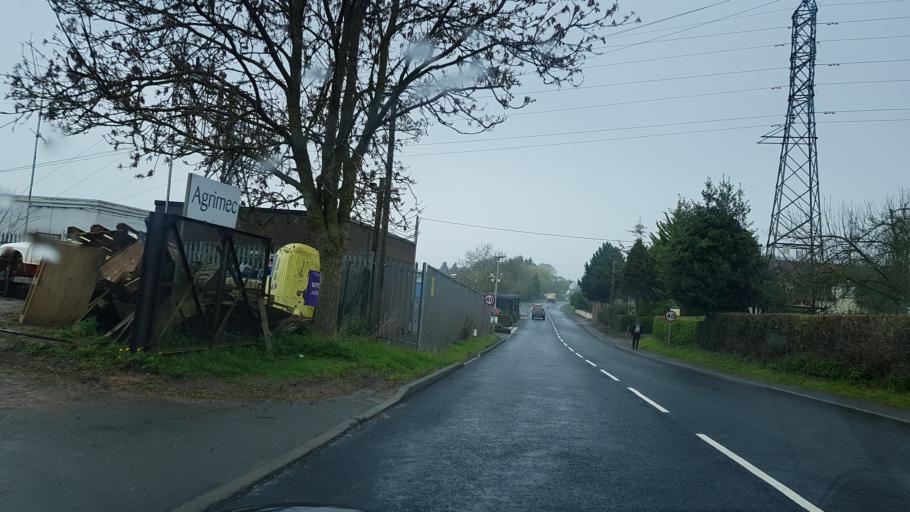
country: GB
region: England
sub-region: Herefordshire
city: Ledbury
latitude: 52.0456
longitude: -2.4266
